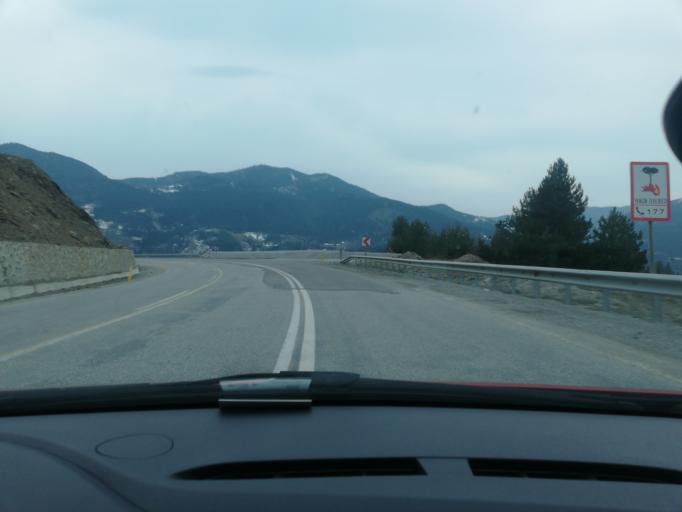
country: TR
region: Kastamonu
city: Kure
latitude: 41.8495
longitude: 33.7140
